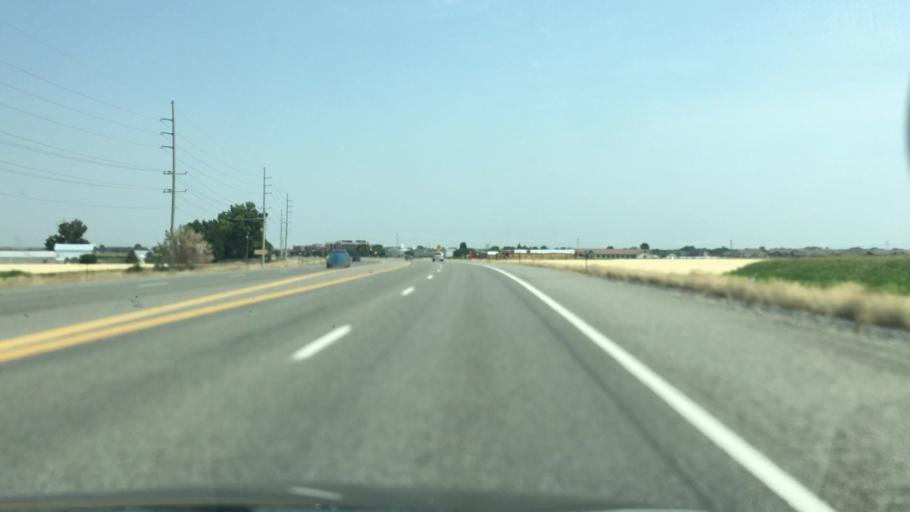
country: US
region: Idaho
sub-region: Twin Falls County
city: Twin Falls
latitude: 42.5923
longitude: -114.5141
